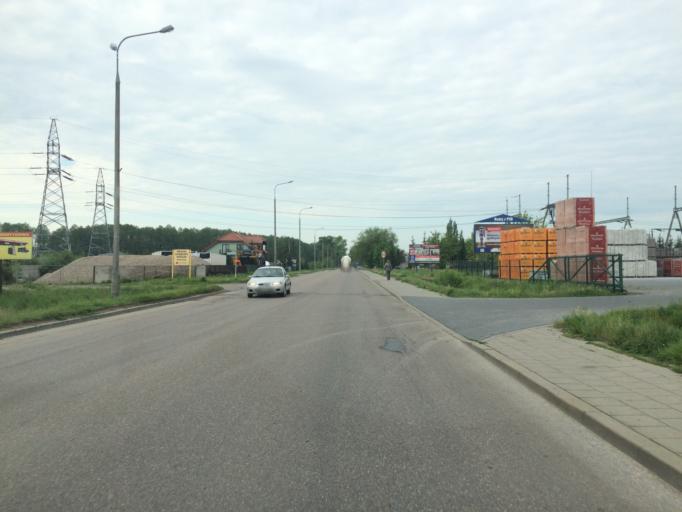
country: PL
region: Masovian Voivodeship
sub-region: Powiat mlawski
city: Mlawa
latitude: 53.1034
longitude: 20.3755
